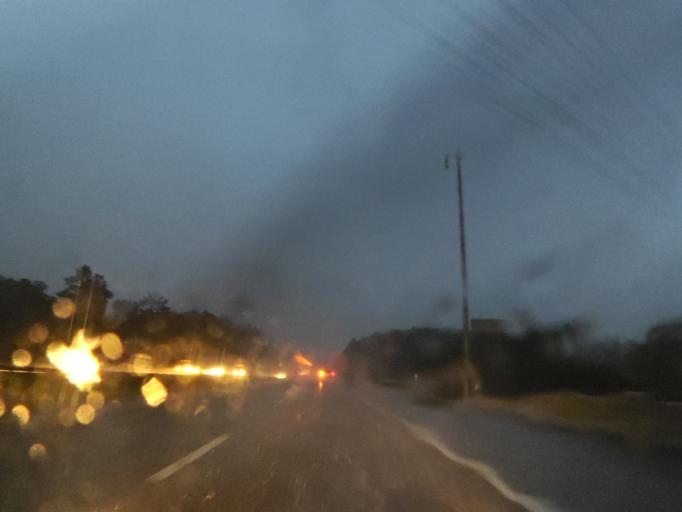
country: US
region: Tennessee
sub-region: Loudon County
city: Lenoir City
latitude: 35.8434
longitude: -84.2707
